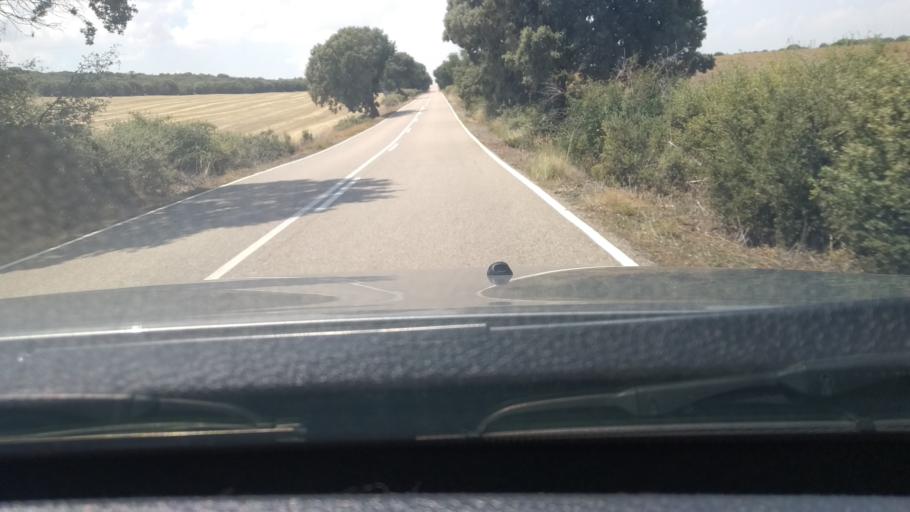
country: ES
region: Castille and Leon
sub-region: Provincia de Burgos
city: Quintanilla de la Mata
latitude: 41.9789
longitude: -3.7951
